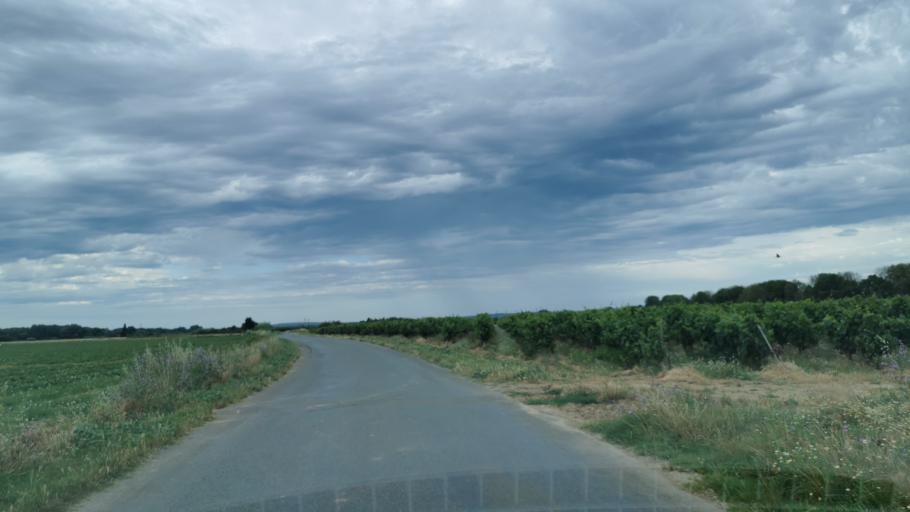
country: FR
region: Languedoc-Roussillon
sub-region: Departement de l'Aude
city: Moussan
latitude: 43.2362
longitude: 2.9899
